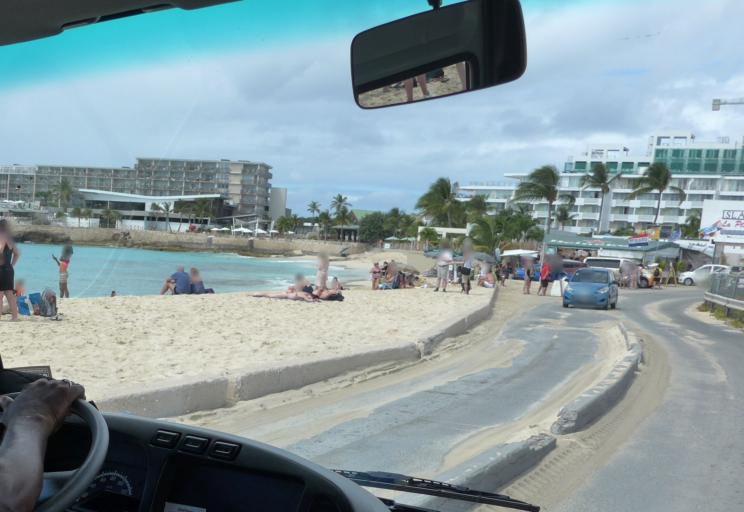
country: MF
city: Marigot
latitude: 18.0396
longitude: -63.1203
